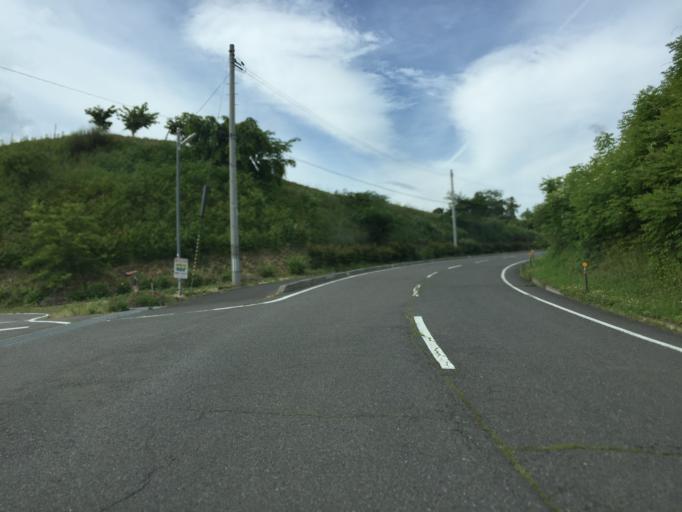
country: JP
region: Fukushima
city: Funehikimachi-funehiki
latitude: 37.4995
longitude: 140.5490
